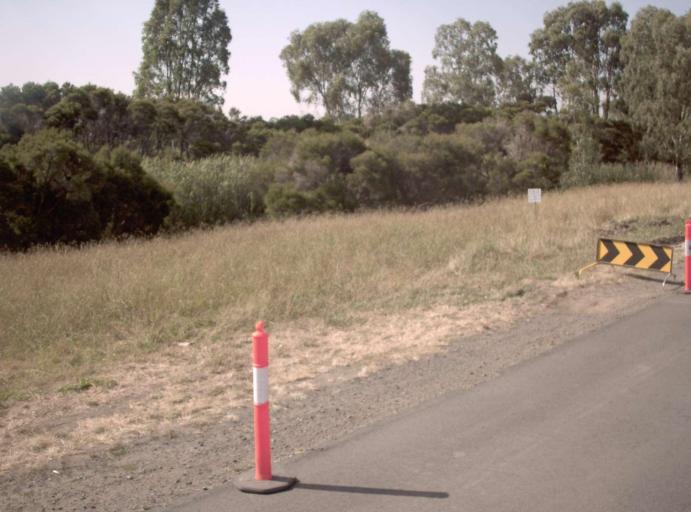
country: AU
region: Victoria
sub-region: Casey
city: Hampton Park
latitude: -38.0173
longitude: 145.2492
